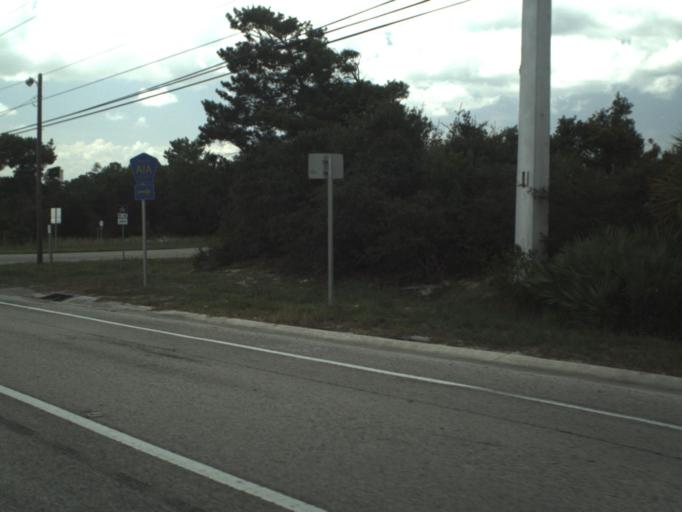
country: US
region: Florida
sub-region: Martin County
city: Hobe Sound
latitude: 27.0456
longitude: -80.1195
